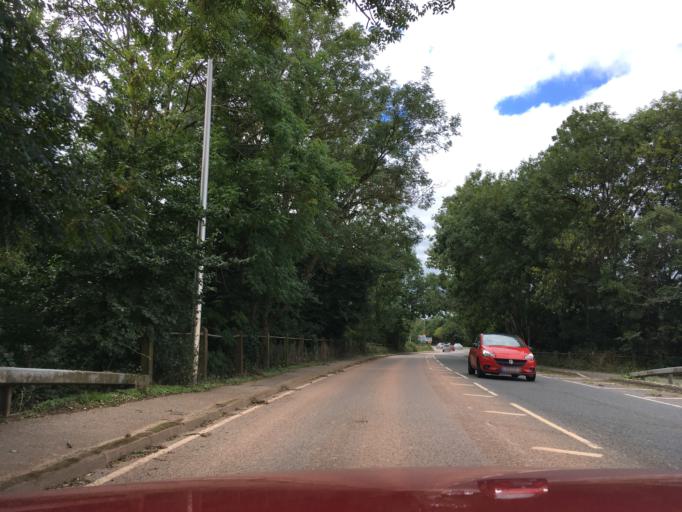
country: GB
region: England
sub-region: Devon
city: Heavitree
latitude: 50.7377
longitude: -3.4732
